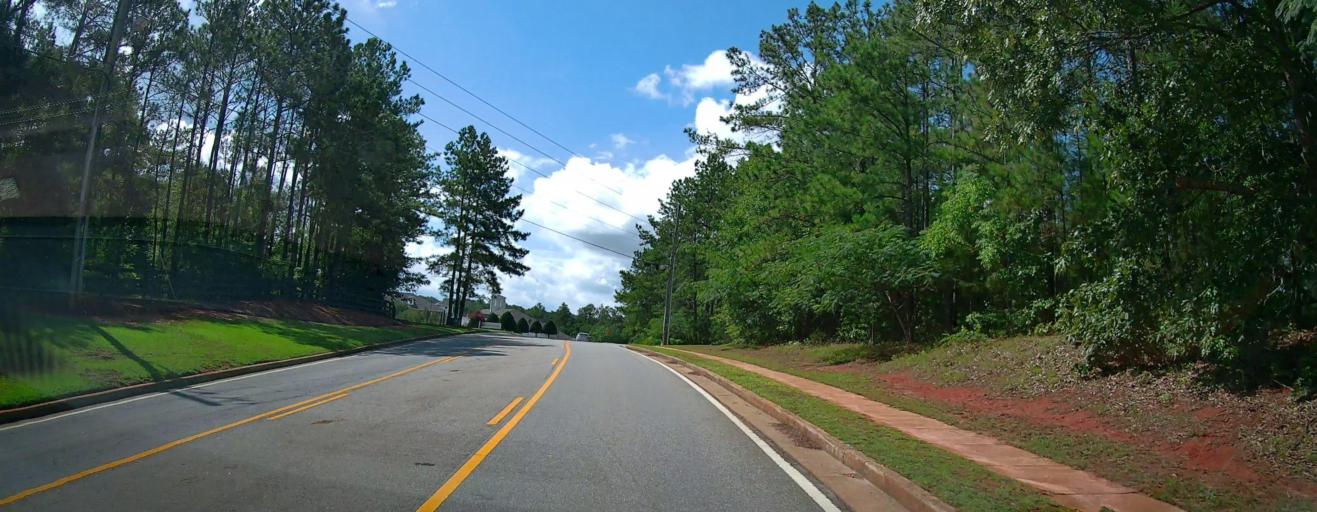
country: US
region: Georgia
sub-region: Houston County
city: Warner Robins
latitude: 32.5883
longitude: -83.6370
